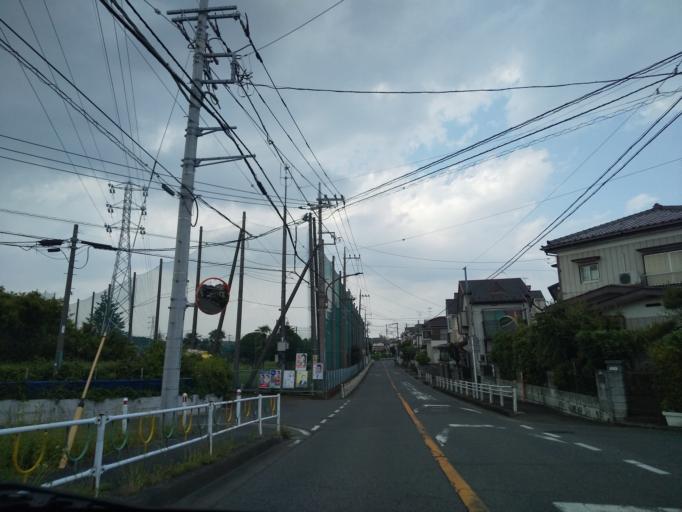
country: JP
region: Tokyo
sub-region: Machida-shi
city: Machida
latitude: 35.5315
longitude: 139.4136
